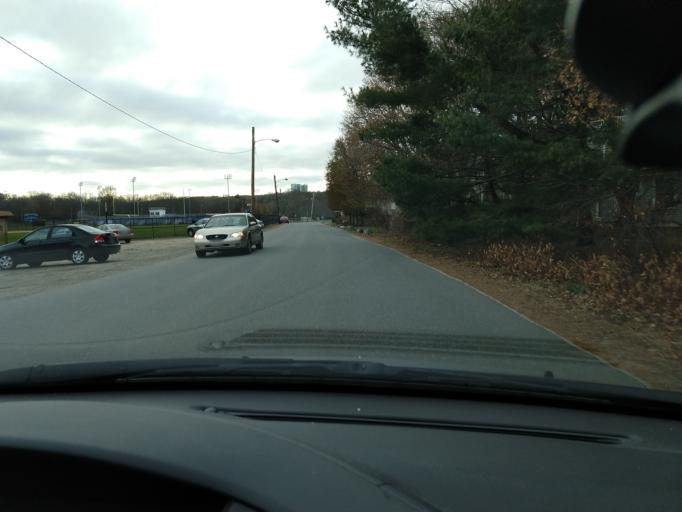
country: US
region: Massachusetts
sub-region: Middlesex County
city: Lexington
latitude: 42.4455
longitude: -71.2326
